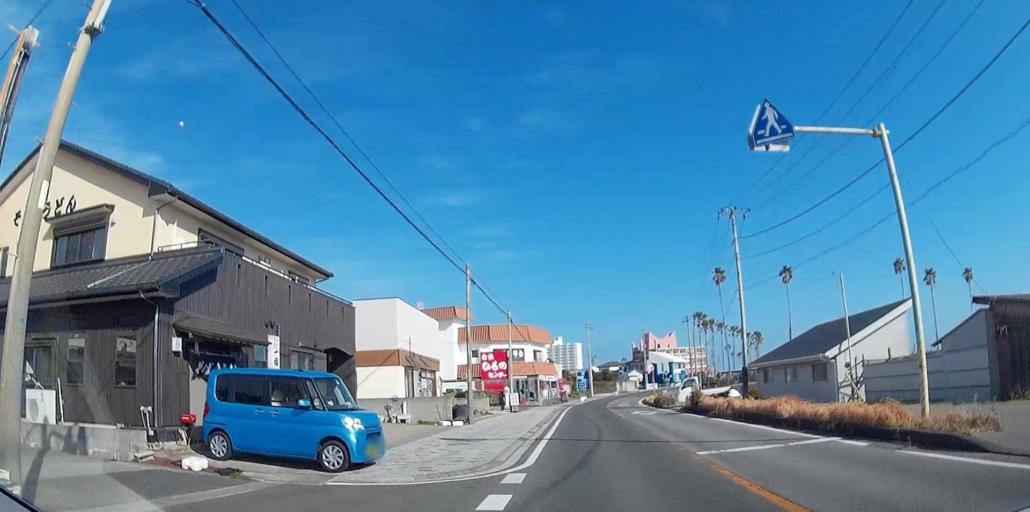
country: JP
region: Chiba
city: Tateyama
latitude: 34.9064
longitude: 139.8937
